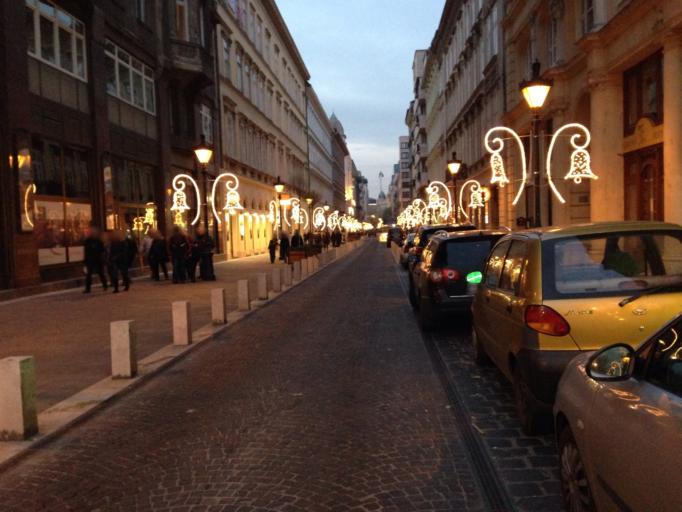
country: HU
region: Budapest
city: Budapest
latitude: 47.4993
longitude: 19.0524
